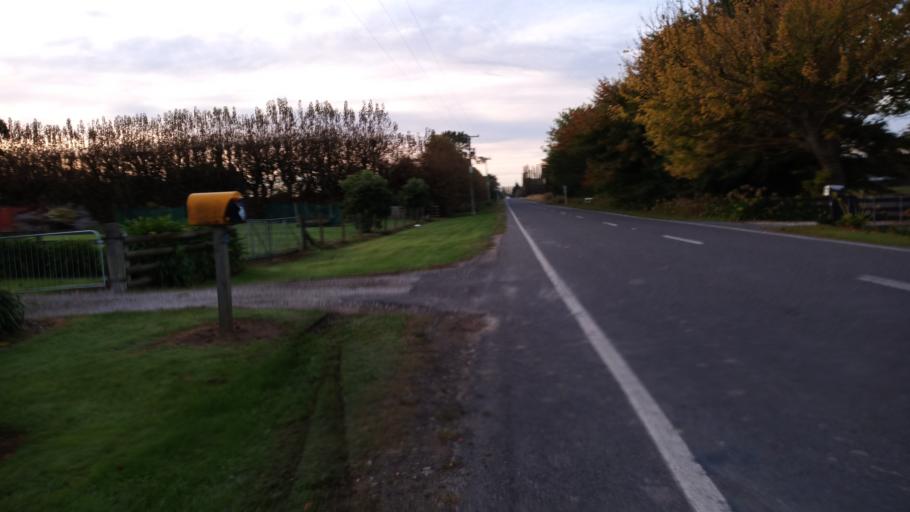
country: NZ
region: Gisborne
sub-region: Gisborne District
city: Gisborne
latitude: -38.6454
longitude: 177.9427
